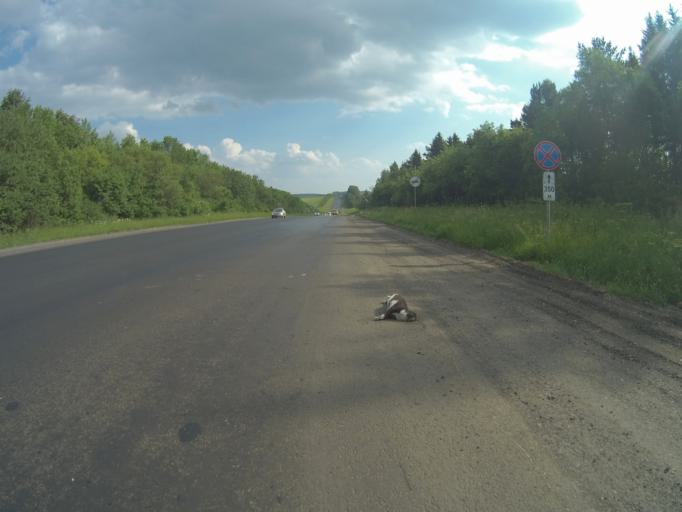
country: RU
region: Vladimir
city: Bogolyubovo
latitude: 56.2788
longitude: 40.4661
